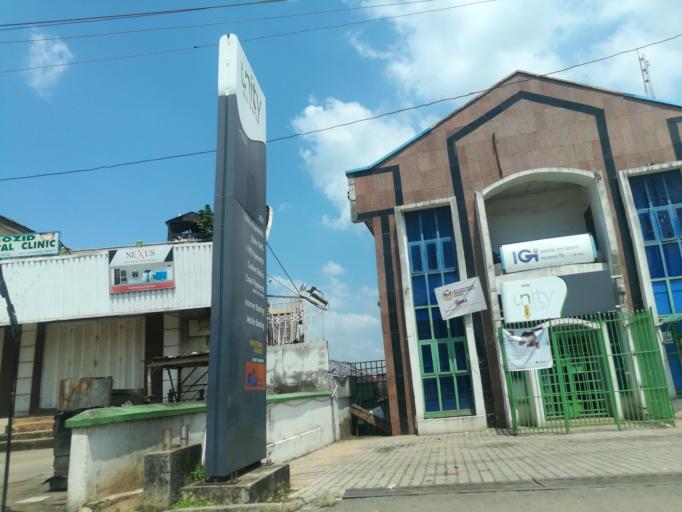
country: NG
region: Oyo
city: Ibadan
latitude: 7.3882
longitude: 3.8824
